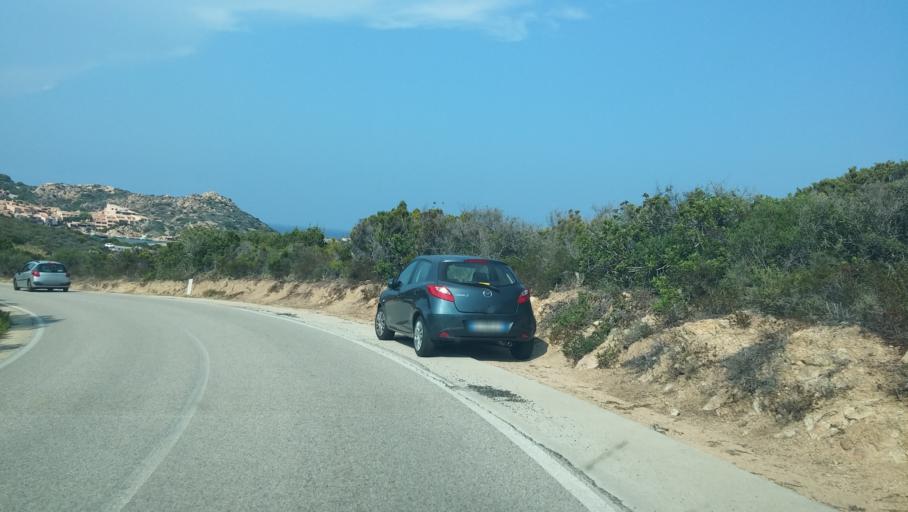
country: IT
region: Sardinia
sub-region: Provincia di Olbia-Tempio
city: La Maddalena
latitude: 41.2529
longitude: 9.4284
